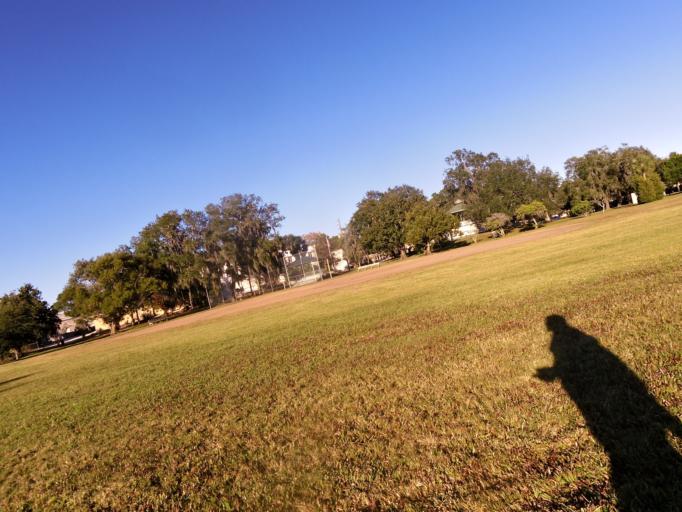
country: US
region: Florida
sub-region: Duval County
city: Jacksonville
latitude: 30.3384
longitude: -81.6589
